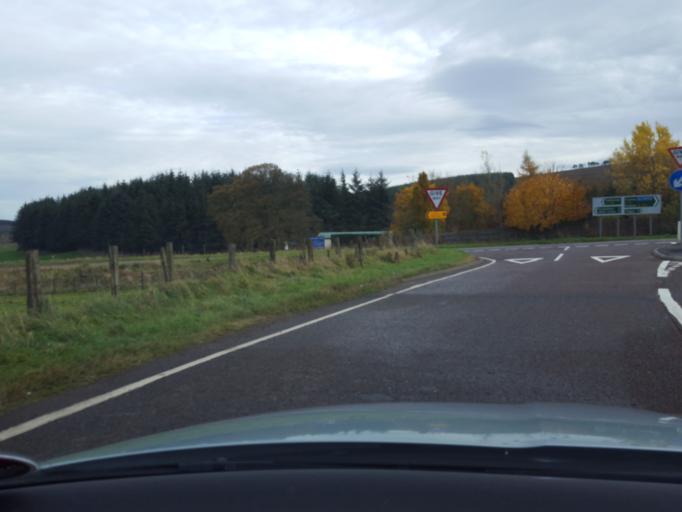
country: GB
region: Scotland
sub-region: South Lanarkshire
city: Biggar
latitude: 55.6835
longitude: -3.4534
